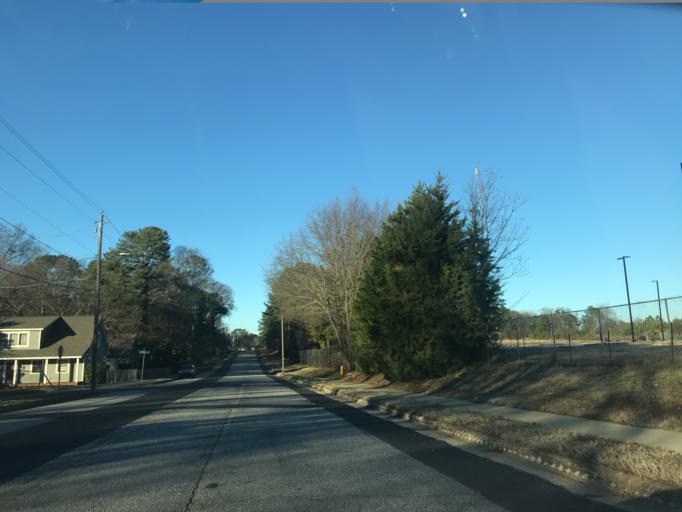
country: US
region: North Carolina
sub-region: Wake County
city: Raleigh
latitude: 35.7895
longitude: -78.6208
